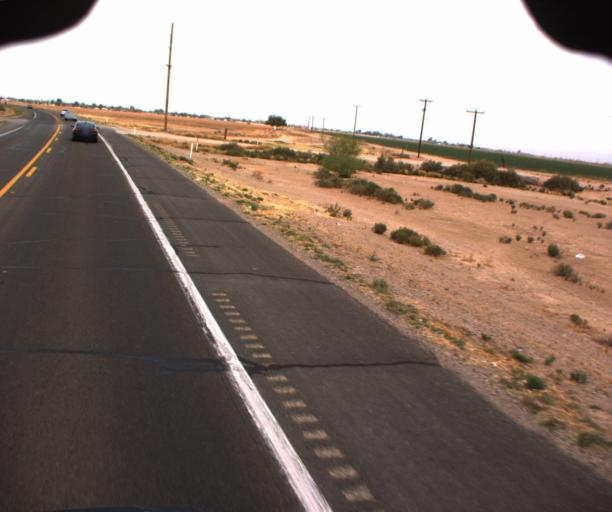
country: US
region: Arizona
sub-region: Pinal County
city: Coolidge
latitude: 32.9437
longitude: -111.5157
